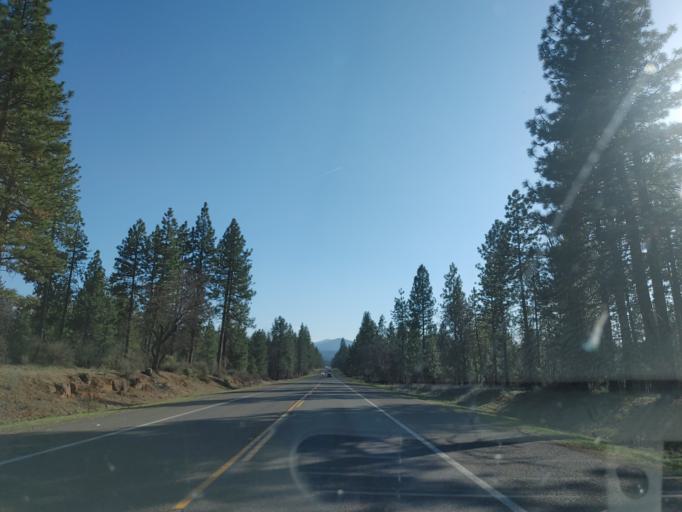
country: US
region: California
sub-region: Shasta County
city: Burney
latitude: 40.9087
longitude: -121.6355
